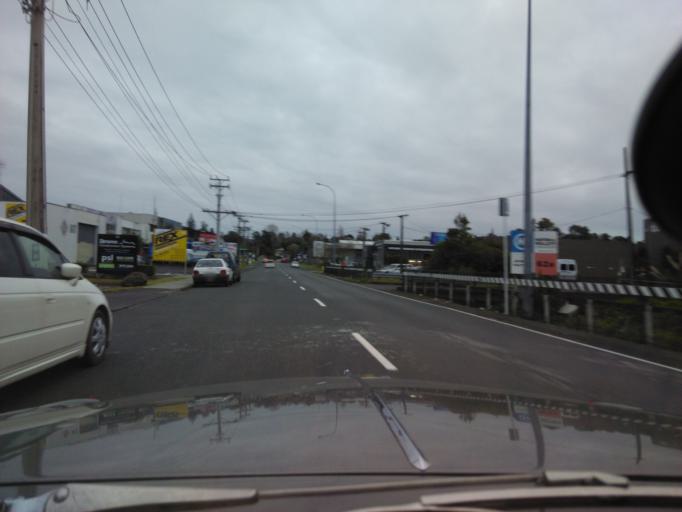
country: NZ
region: Auckland
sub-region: Auckland
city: North Shore
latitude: -36.7741
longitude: 174.7343
